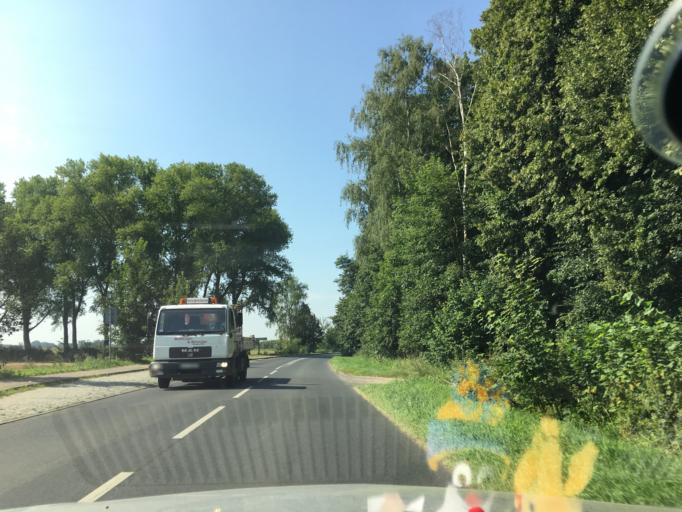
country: PL
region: West Pomeranian Voivodeship
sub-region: Powiat kamienski
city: Kamien Pomorski
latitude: 54.0017
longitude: 14.8358
